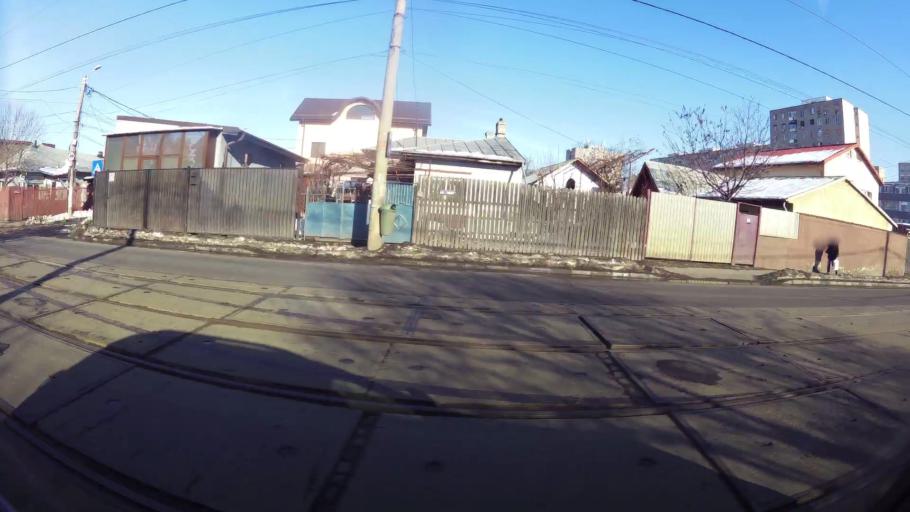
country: RO
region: Bucuresti
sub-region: Municipiul Bucuresti
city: Bucuresti
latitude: 44.3849
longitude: 26.0802
